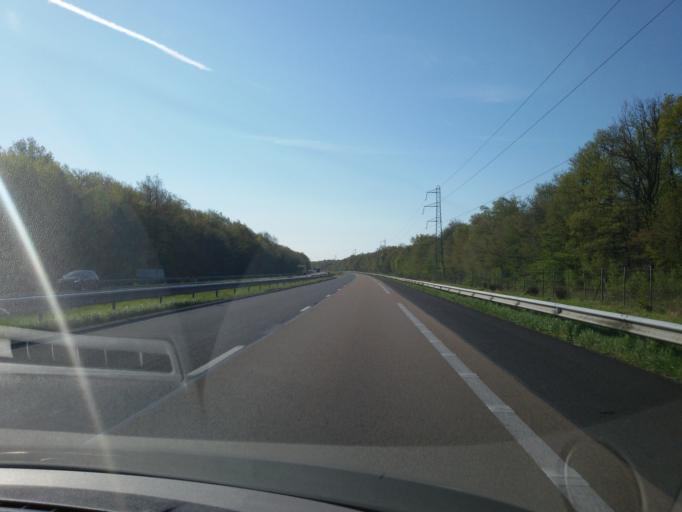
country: FR
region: Centre
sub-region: Departement du Loiret
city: Courtenay
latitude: 48.0903
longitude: 3.0382
